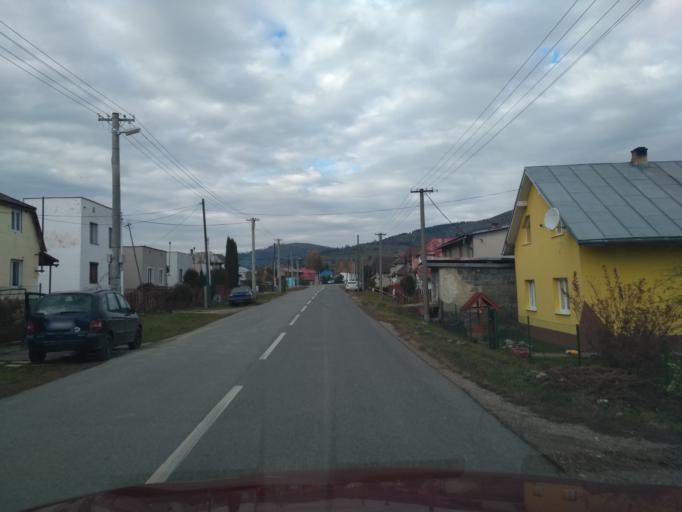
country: SK
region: Kosicky
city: Krompachy
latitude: 48.8061
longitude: 20.7263
